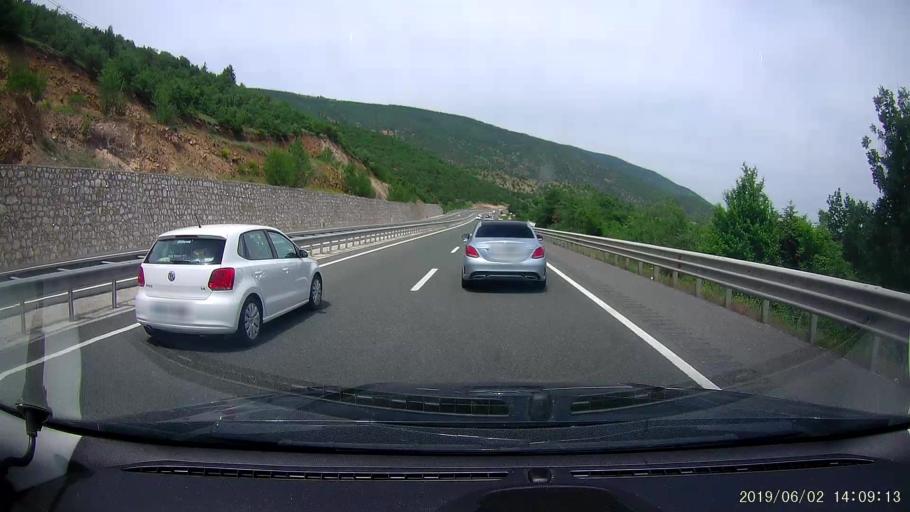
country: TR
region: Cankiri
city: Ilgaz
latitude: 40.8920
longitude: 33.7393
